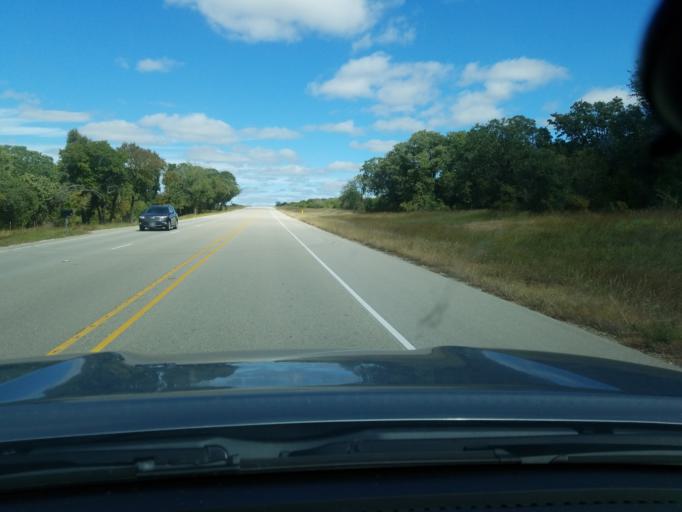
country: US
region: Texas
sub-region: Hamilton County
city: Hamilton
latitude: 31.6193
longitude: -98.1576
